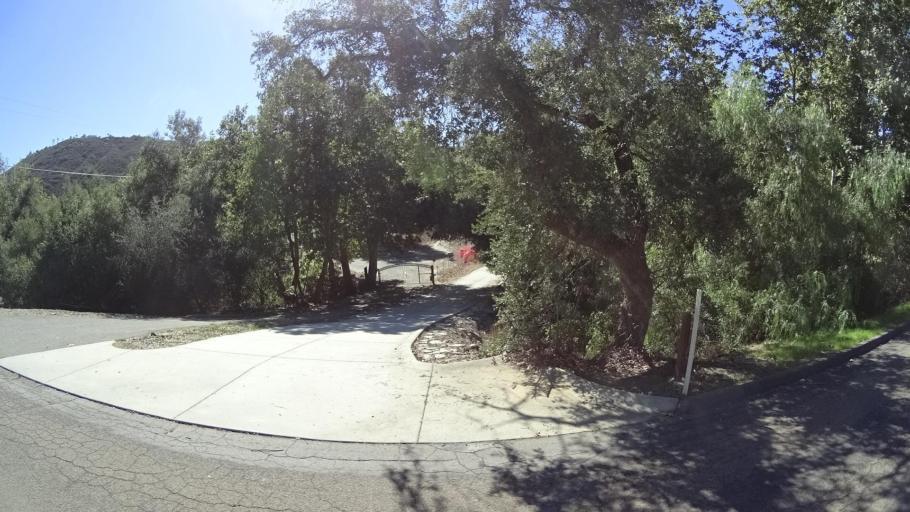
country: US
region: California
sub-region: San Diego County
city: Alpine
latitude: 32.8590
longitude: -116.7724
